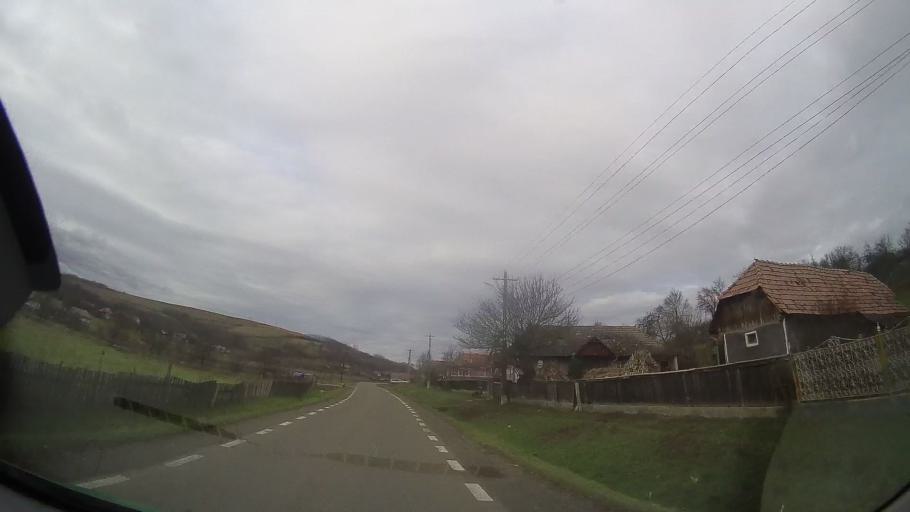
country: RO
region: Mures
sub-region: Comuna Cozma
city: Cozma
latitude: 46.8037
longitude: 24.5307
